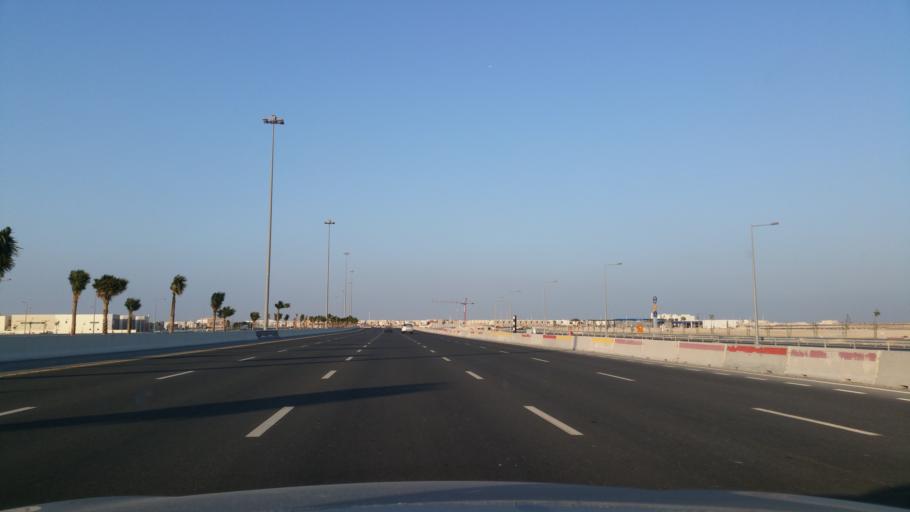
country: QA
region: Al Khawr
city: Al Khawr
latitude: 25.6538
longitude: 51.4980
